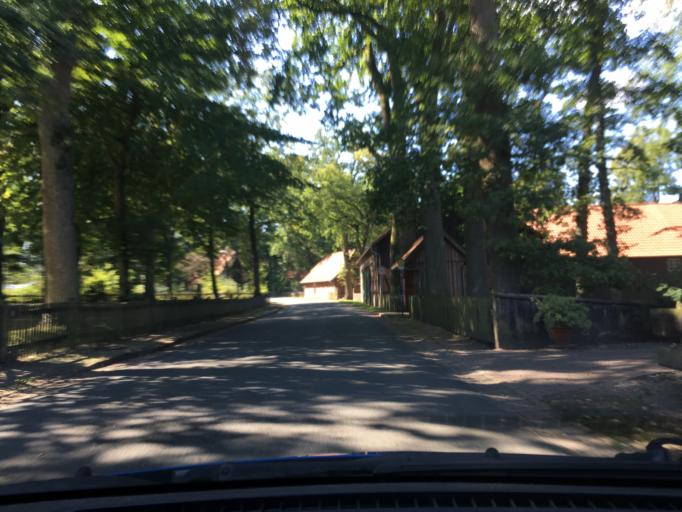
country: DE
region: Lower Saxony
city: Bergen
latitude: 52.8320
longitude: 9.9376
